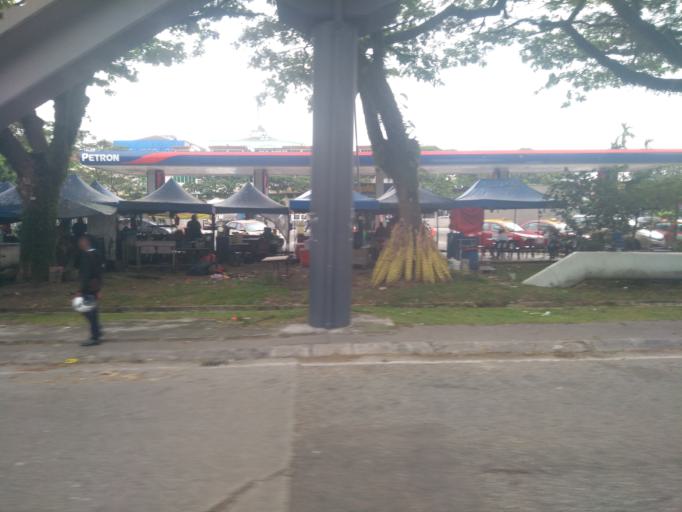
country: MY
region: Johor
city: Skudai
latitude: 1.5084
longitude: 103.6892
